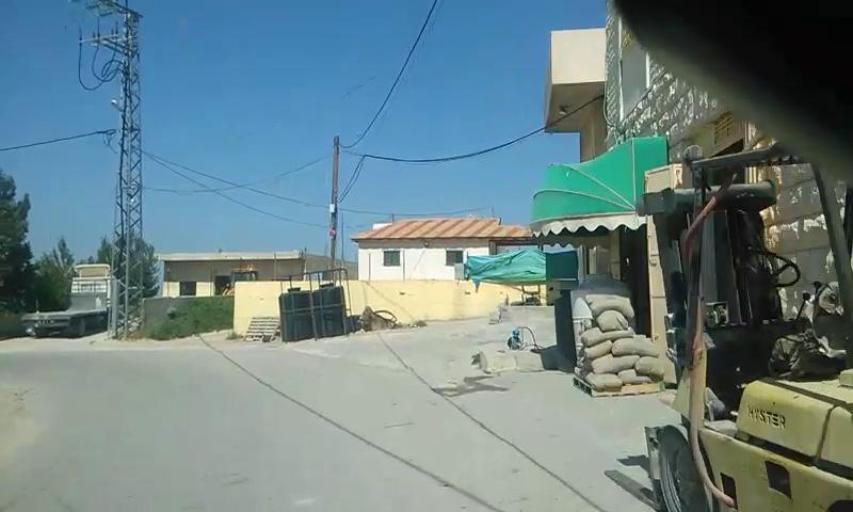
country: PS
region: West Bank
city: Al Majd
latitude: 31.4819
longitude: 34.9498
